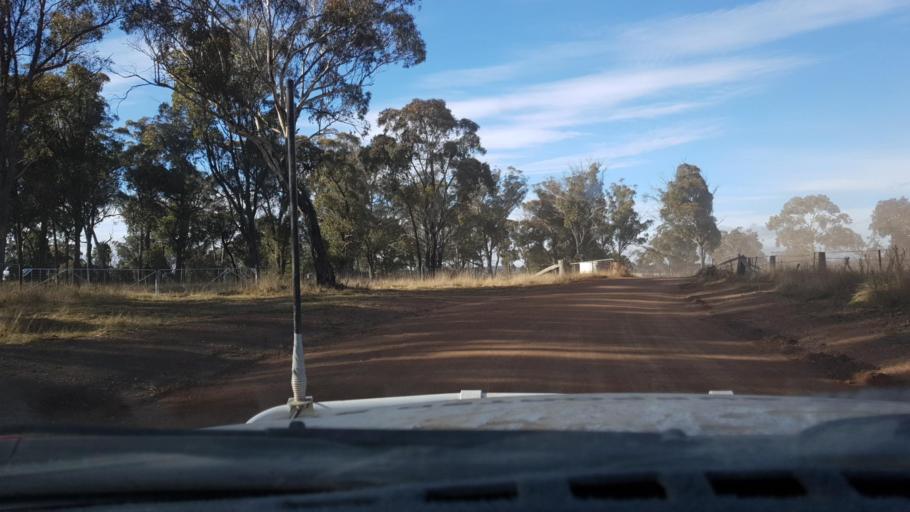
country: AU
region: New South Wales
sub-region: Armidale Dumaresq
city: Enmore
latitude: -30.7432
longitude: 151.6037
